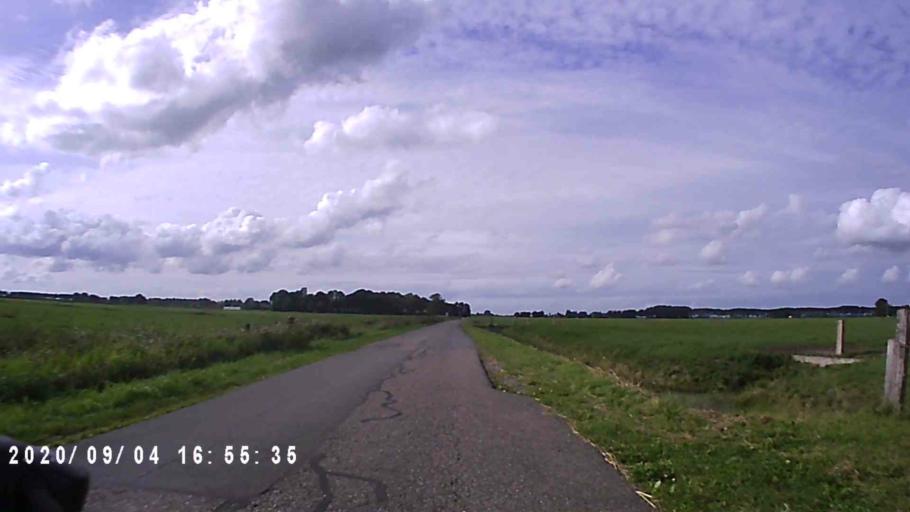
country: NL
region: Groningen
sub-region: Gemeente Zuidhorn
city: Aduard
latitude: 53.2640
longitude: 6.5180
